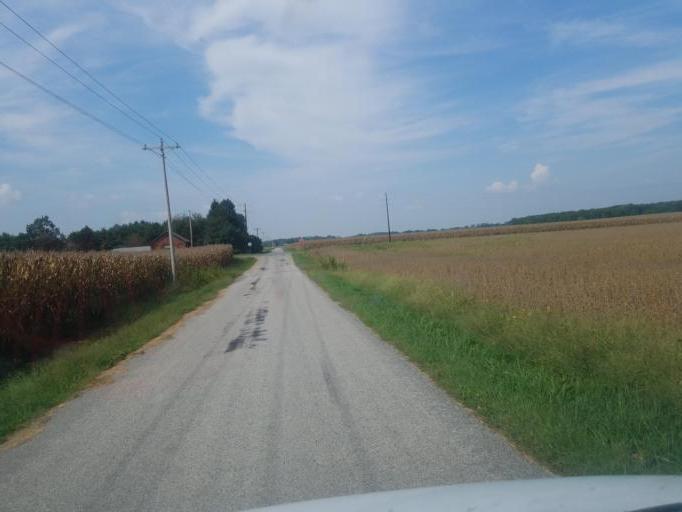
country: US
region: Ohio
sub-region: Wyandot County
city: Upper Sandusky
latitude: 40.6585
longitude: -83.2921
